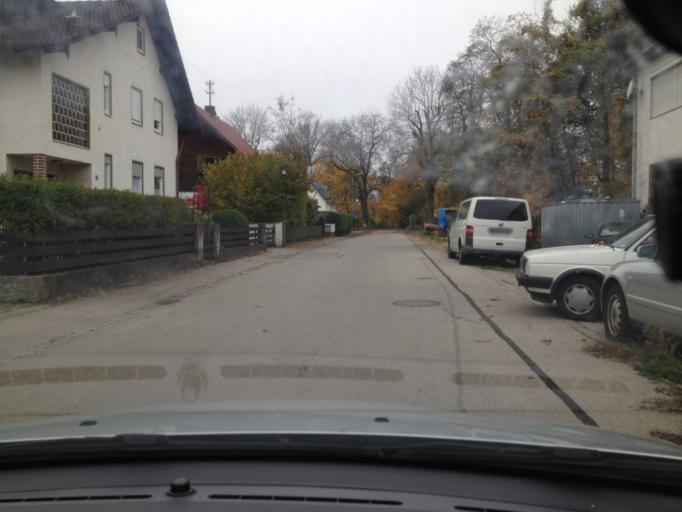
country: DE
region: Bavaria
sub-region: Swabia
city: Ettringen
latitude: 48.1083
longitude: 10.6669
